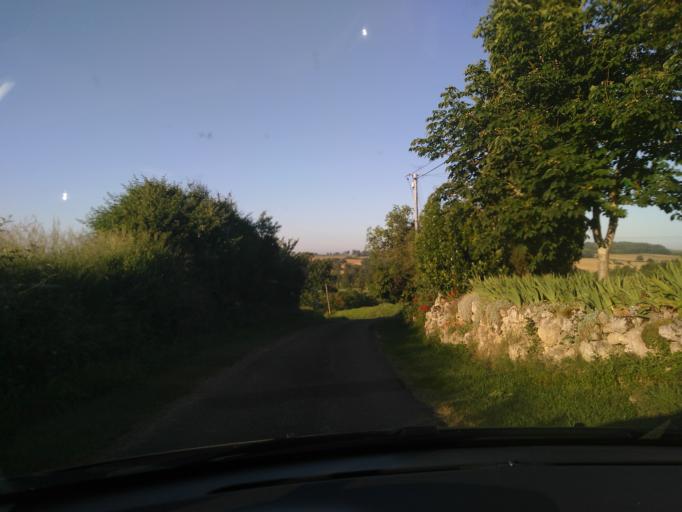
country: FR
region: Midi-Pyrenees
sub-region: Departement du Gers
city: Valence-sur-Baise
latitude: 43.8736
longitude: 0.4565
